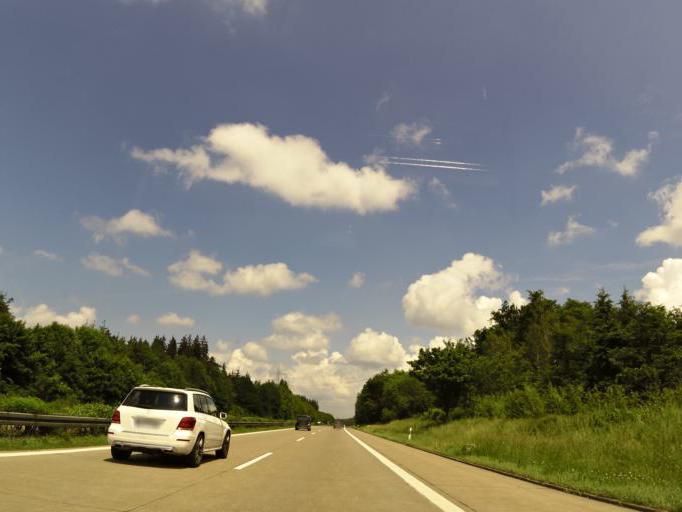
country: DE
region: Baden-Wuerttemberg
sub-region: Regierungsbezirk Stuttgart
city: Nattheim
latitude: 48.7526
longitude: 10.2013
